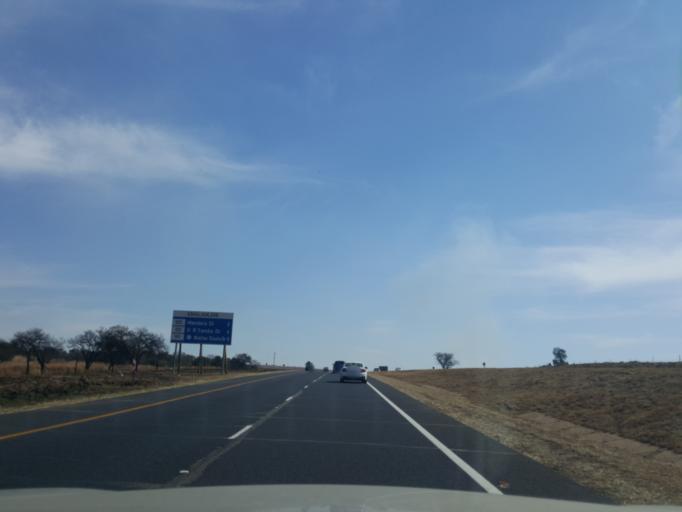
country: ZA
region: Mpumalanga
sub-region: Nkangala District Municipality
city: Witbank
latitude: -25.8783
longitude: 29.2956
